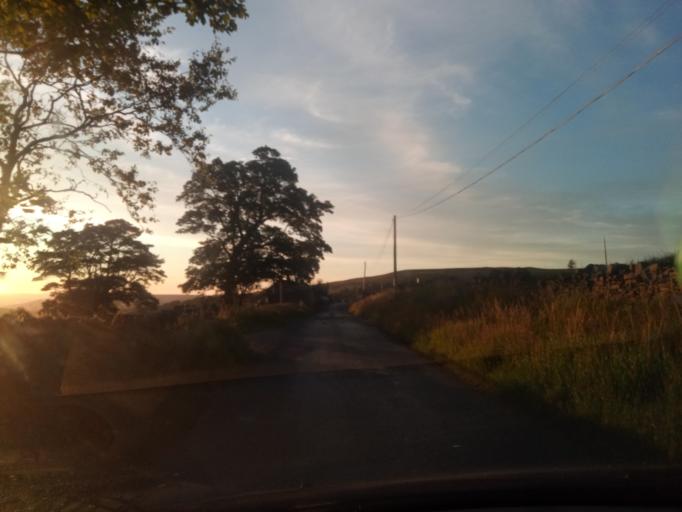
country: GB
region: England
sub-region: Northumberland
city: Bardon Mill
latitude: 54.7909
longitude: -2.3412
